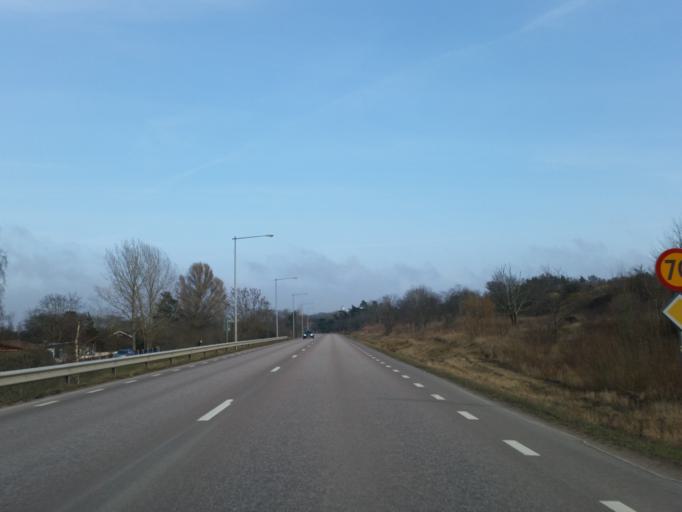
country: SE
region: Kalmar
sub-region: Borgholms Kommun
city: Borgholm
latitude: 56.8785
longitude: 16.6940
